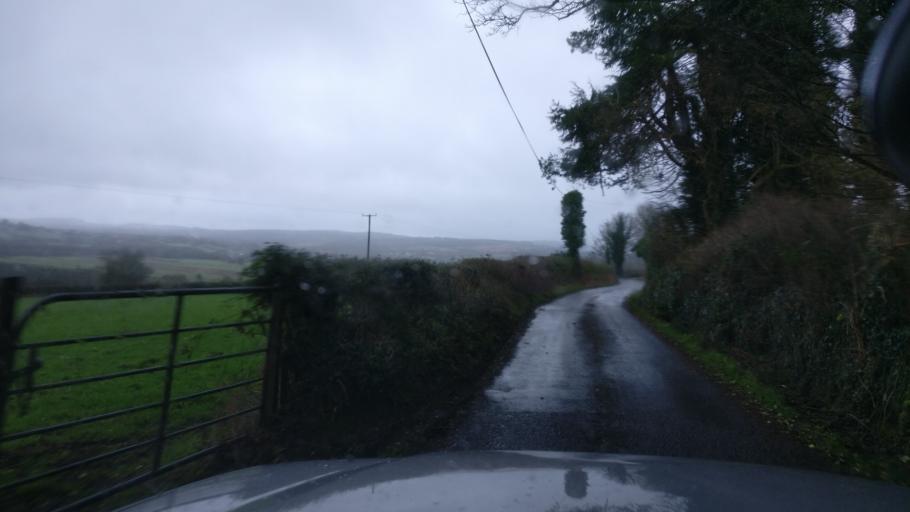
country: IE
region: Connaught
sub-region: County Galway
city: Loughrea
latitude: 53.1678
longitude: -8.6433
